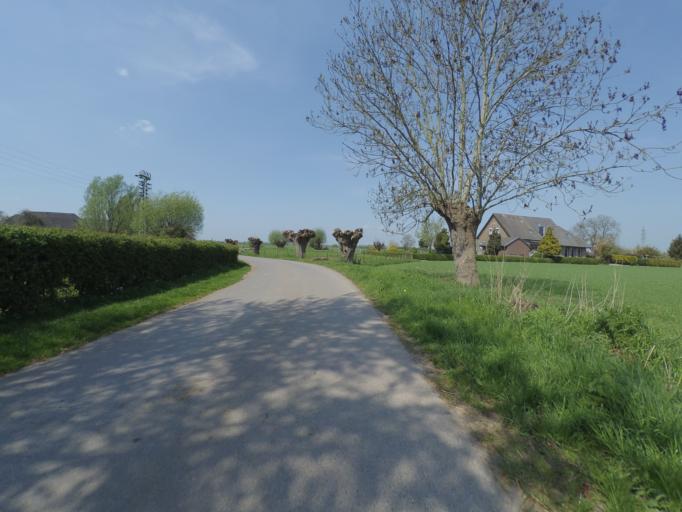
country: NL
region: Gelderland
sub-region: Oude IJsselstreek
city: Gendringen
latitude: 51.8279
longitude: 6.3481
